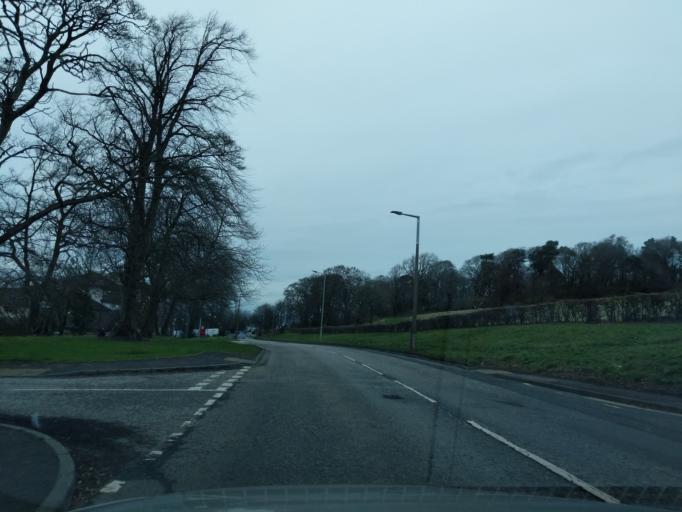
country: GB
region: Scotland
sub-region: Edinburgh
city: Colinton
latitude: 55.9546
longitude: -3.2785
